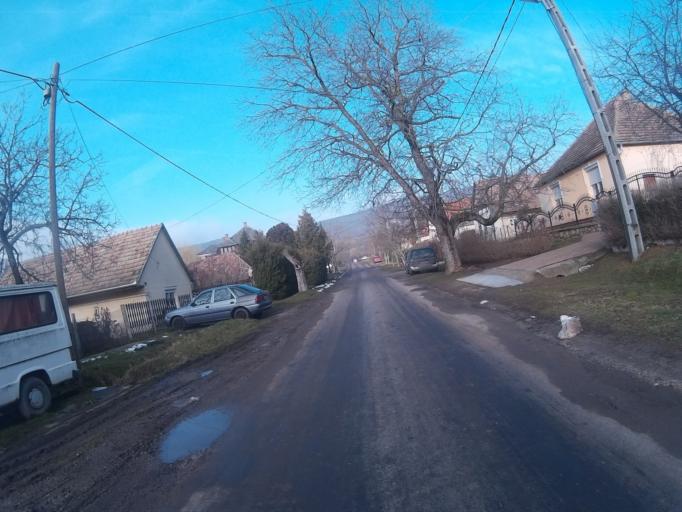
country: HU
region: Komarom-Esztergom
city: Tarjan
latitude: 47.6492
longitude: 18.5061
